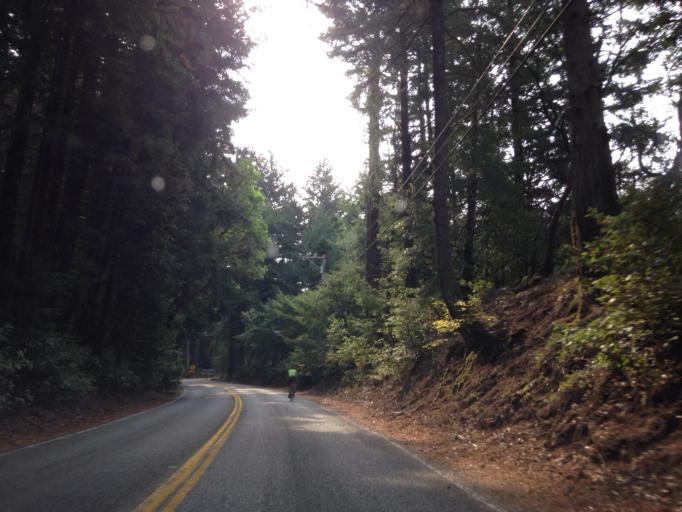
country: US
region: California
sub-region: San Mateo County
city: Woodside
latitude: 37.4009
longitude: -122.2973
